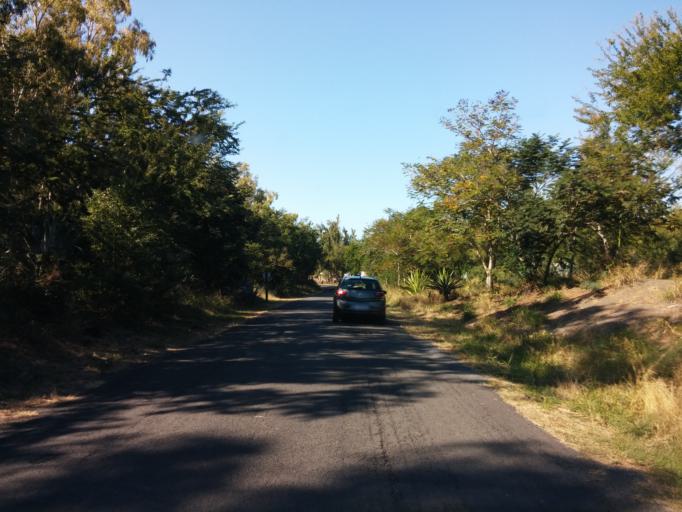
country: RE
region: Reunion
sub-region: Reunion
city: Les Avirons
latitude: -21.2746
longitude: 55.3547
